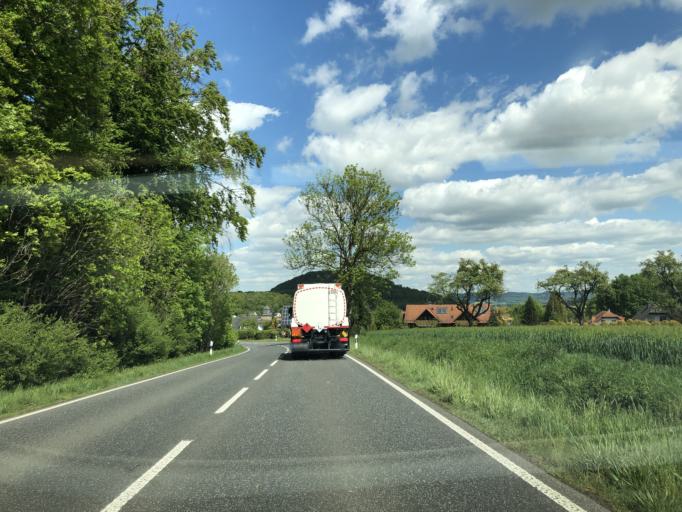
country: DE
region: Hesse
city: Felsberg
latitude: 51.1749
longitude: 9.4079
